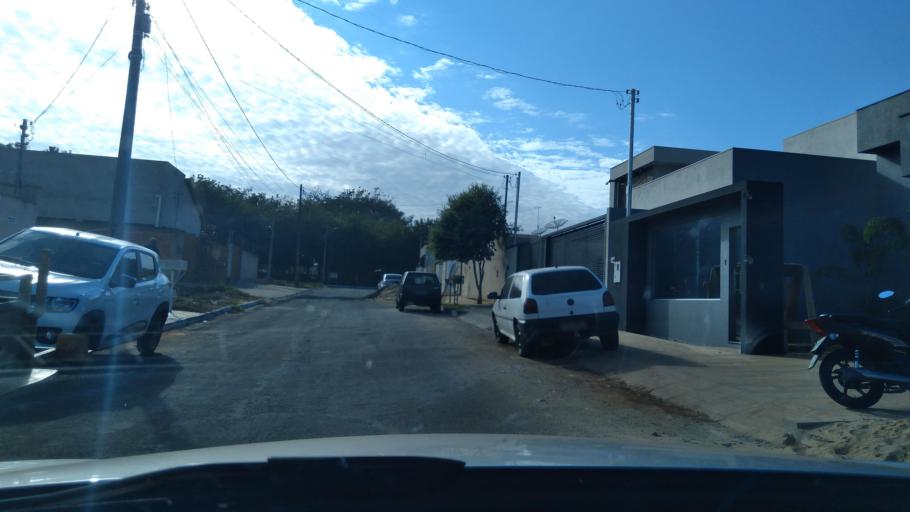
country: BR
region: Goias
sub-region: Mineiros
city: Mineiros
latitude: -17.5543
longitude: -52.5586
